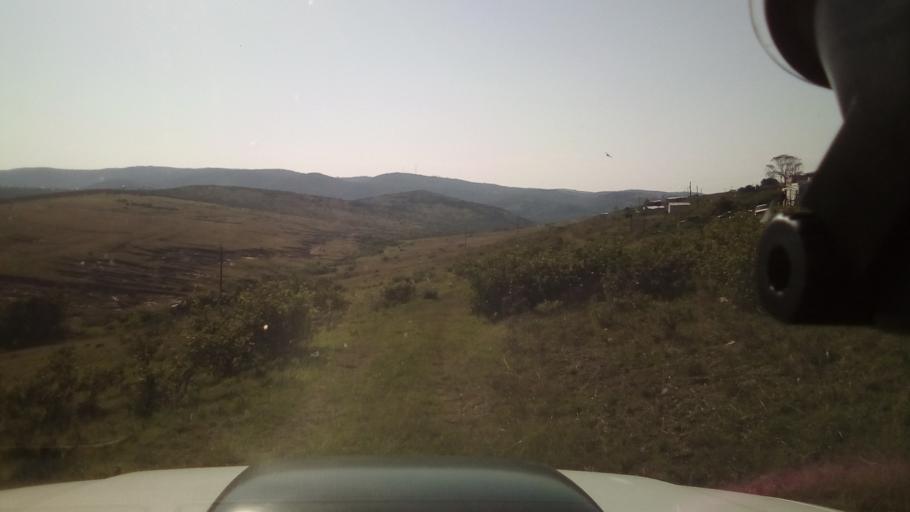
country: ZA
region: Eastern Cape
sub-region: Buffalo City Metropolitan Municipality
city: East London
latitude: -32.8399
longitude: 27.9913
